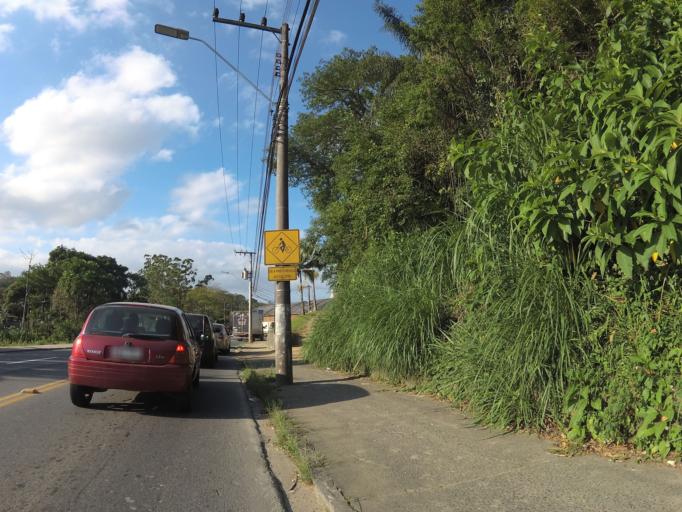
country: BR
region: Santa Catarina
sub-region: Blumenau
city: Blumenau
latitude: -26.9197
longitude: -49.0944
